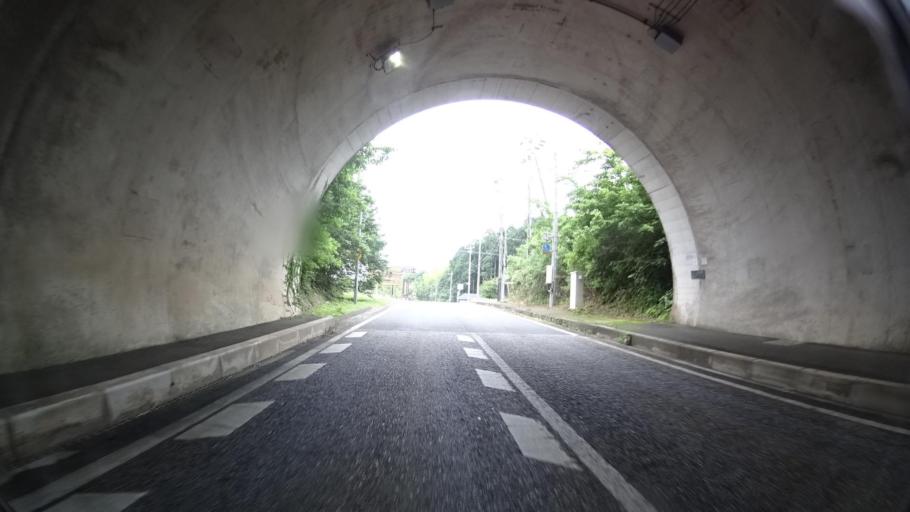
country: JP
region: Kyoto
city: Maizuru
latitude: 35.5272
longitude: 135.3458
